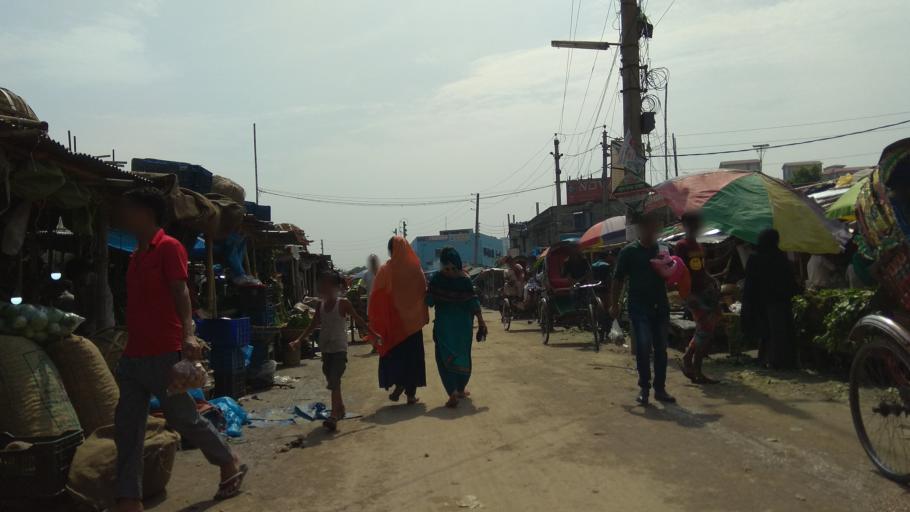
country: BD
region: Dhaka
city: Paltan
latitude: 23.8081
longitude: 90.3833
